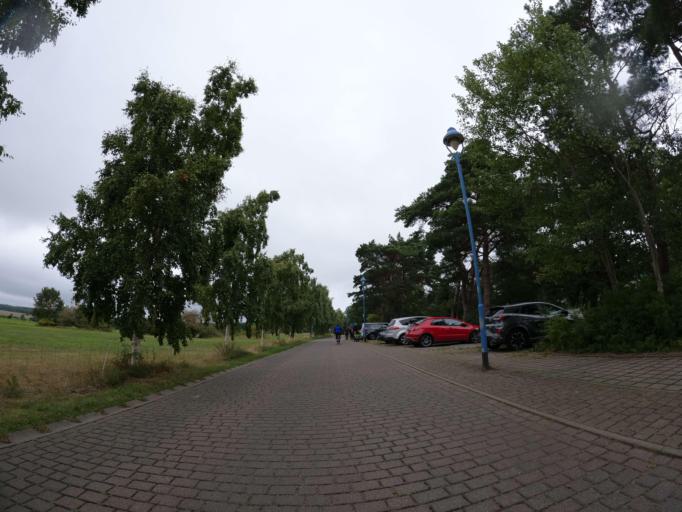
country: DE
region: Mecklenburg-Vorpommern
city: Ostseebad Gohren
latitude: 54.3295
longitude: 13.7292
